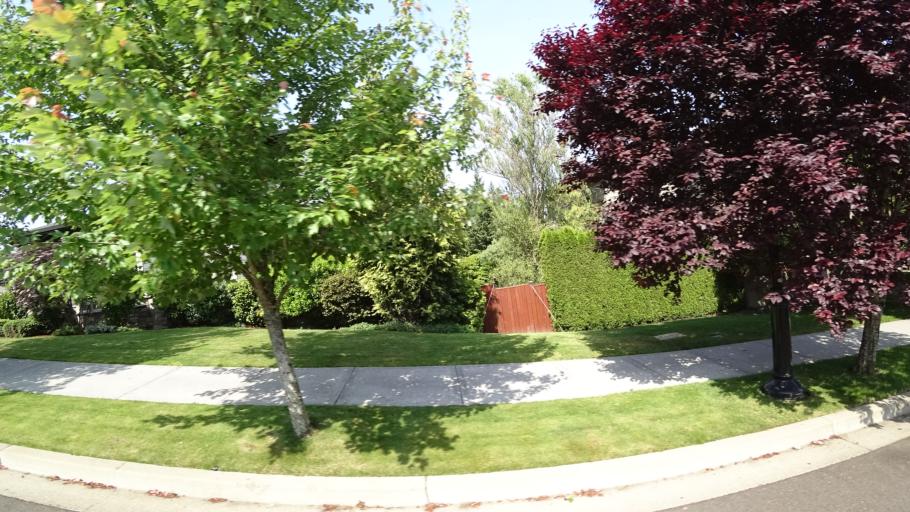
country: US
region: Oregon
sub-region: Clackamas County
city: Happy Valley
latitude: 45.4546
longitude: -122.5096
